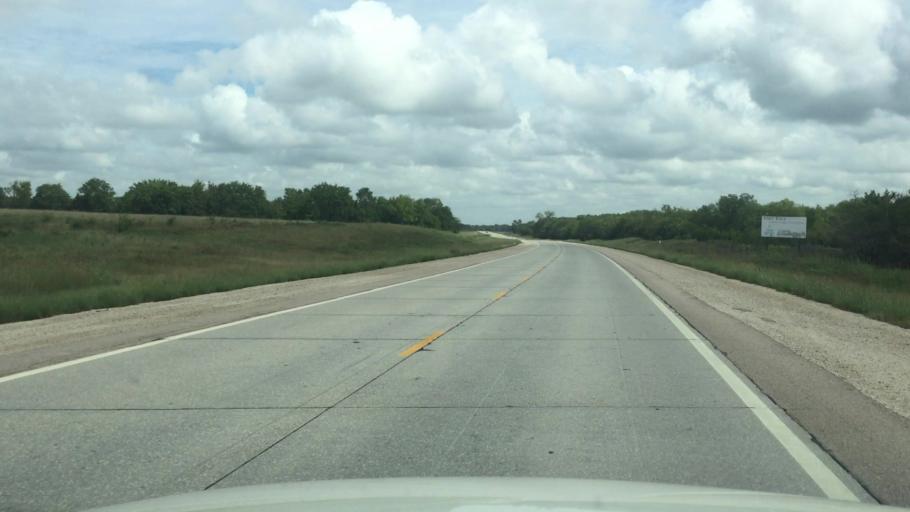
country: US
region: Kansas
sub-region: Allen County
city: Iola
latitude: 37.8978
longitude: -95.3834
